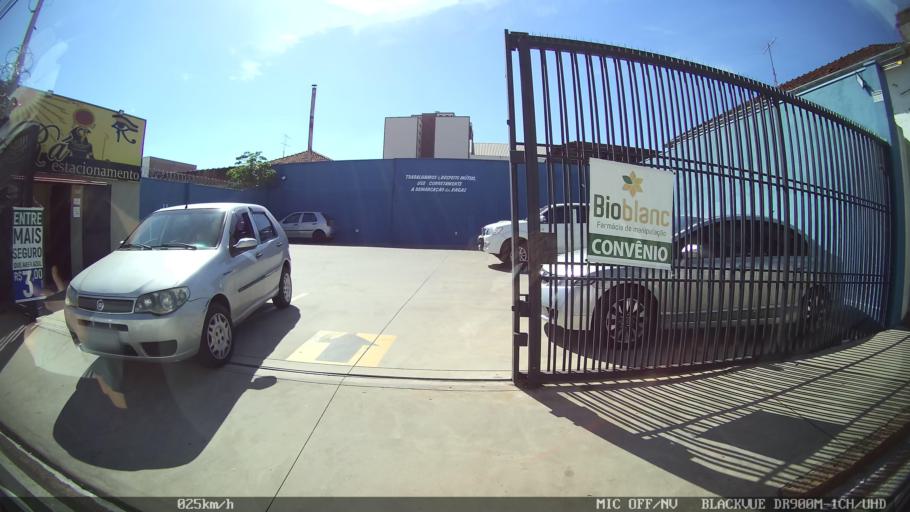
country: BR
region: Sao Paulo
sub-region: Franca
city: Franca
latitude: -20.5346
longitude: -47.4017
